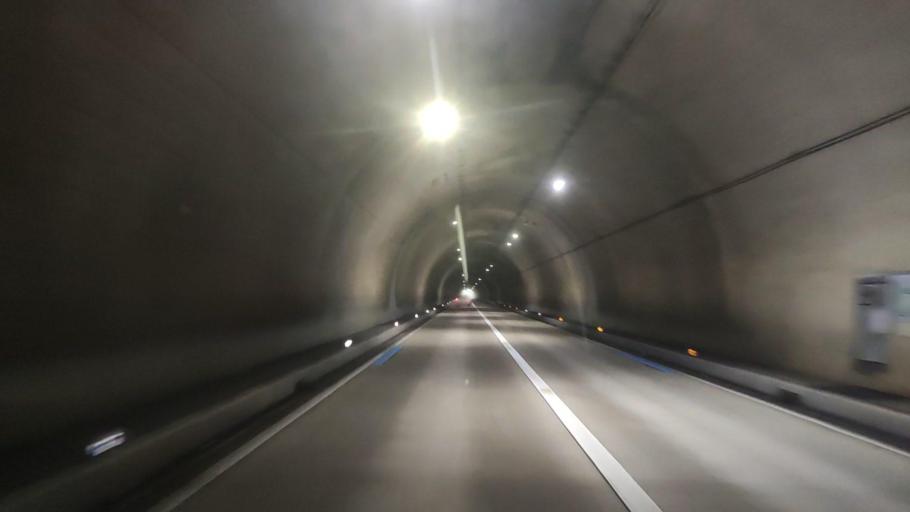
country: JP
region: Wakayama
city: Tanabe
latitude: 33.8342
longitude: 135.6569
